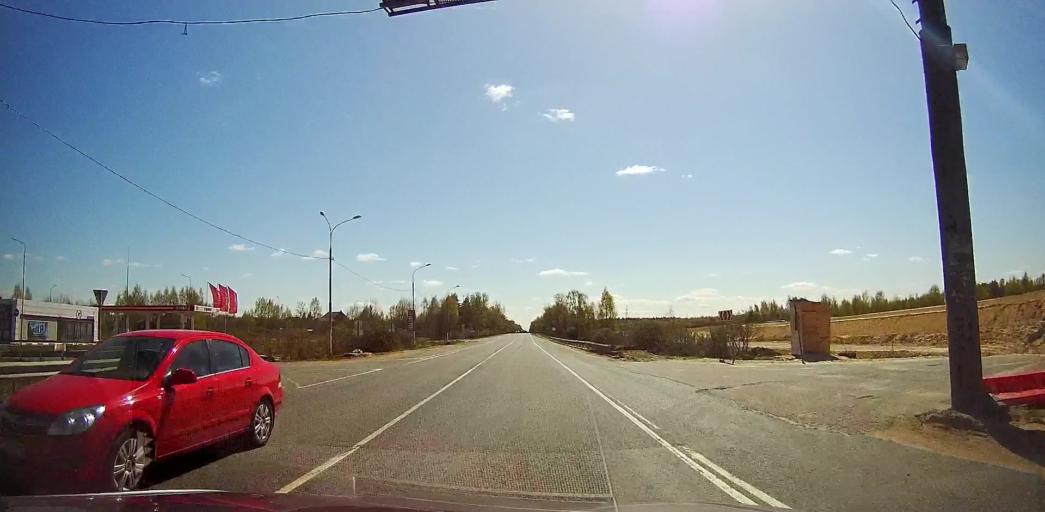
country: RU
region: Moskovskaya
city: Gzhel'
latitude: 55.5760
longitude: 38.3895
